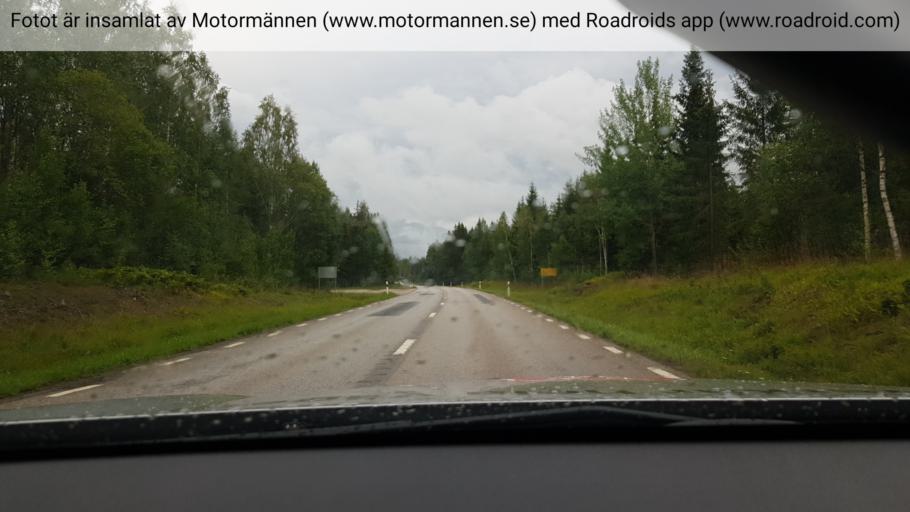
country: SE
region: Uppsala
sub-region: Alvkarleby Kommun
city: AElvkarleby
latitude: 60.5567
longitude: 17.4725
